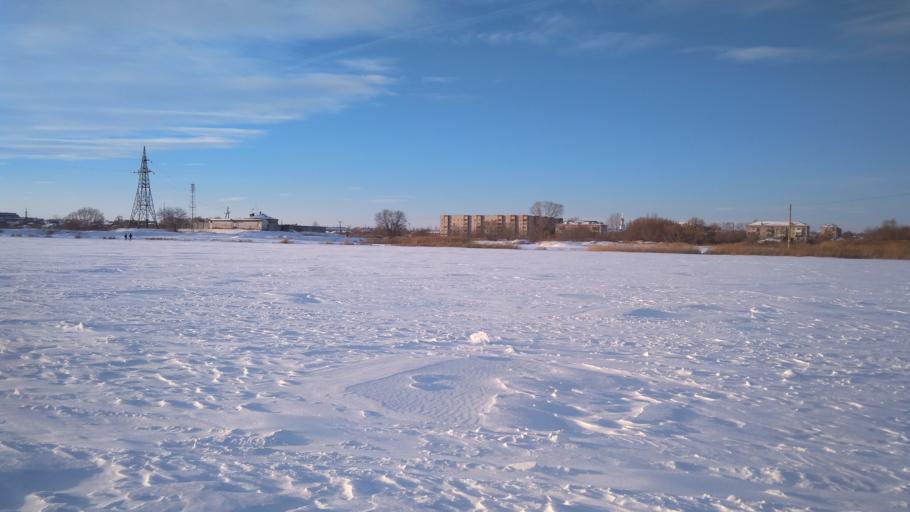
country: RU
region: Chelyabinsk
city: Troitsk
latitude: 54.0810
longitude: 61.5815
